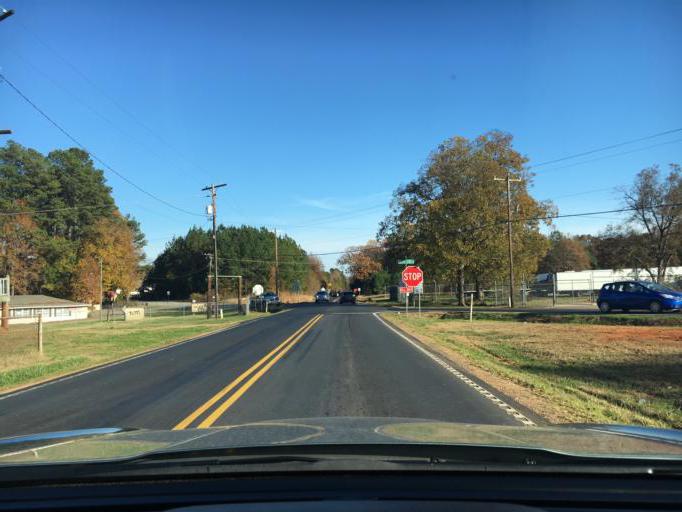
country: US
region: South Carolina
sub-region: Spartanburg County
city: Inman
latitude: 34.9975
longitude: -82.0560
